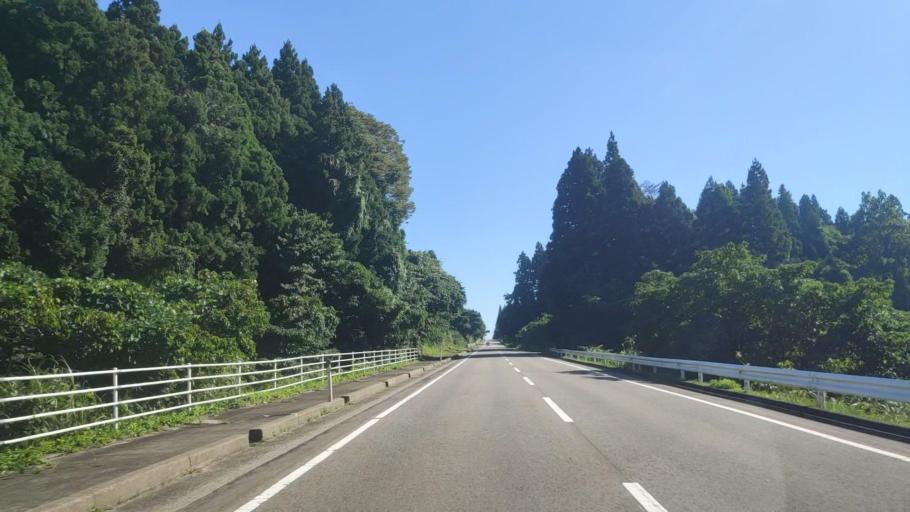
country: JP
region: Ishikawa
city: Nanao
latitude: 37.3745
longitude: 137.2346
